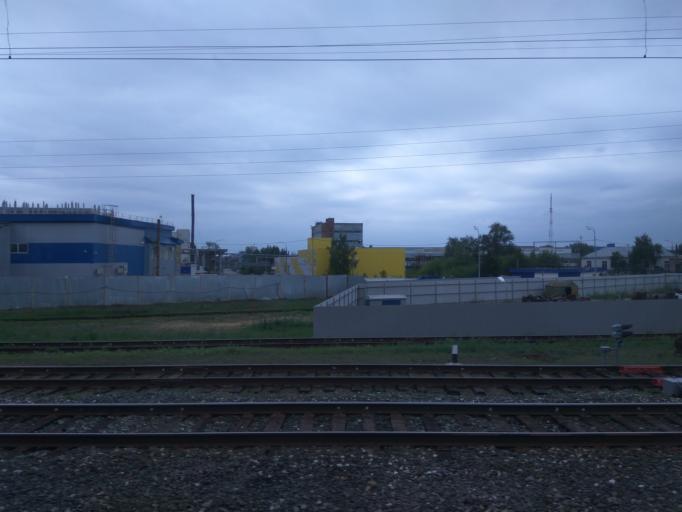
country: RU
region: Tatarstan
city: Staroye Arakchino
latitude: 55.8386
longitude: 49.0355
